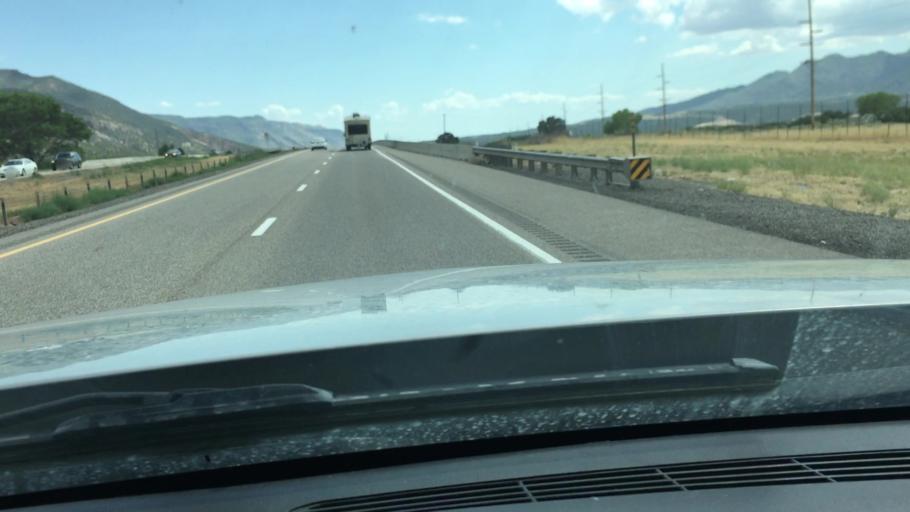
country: US
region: Utah
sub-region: Washington County
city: Toquerville
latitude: 37.4643
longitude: -113.2257
